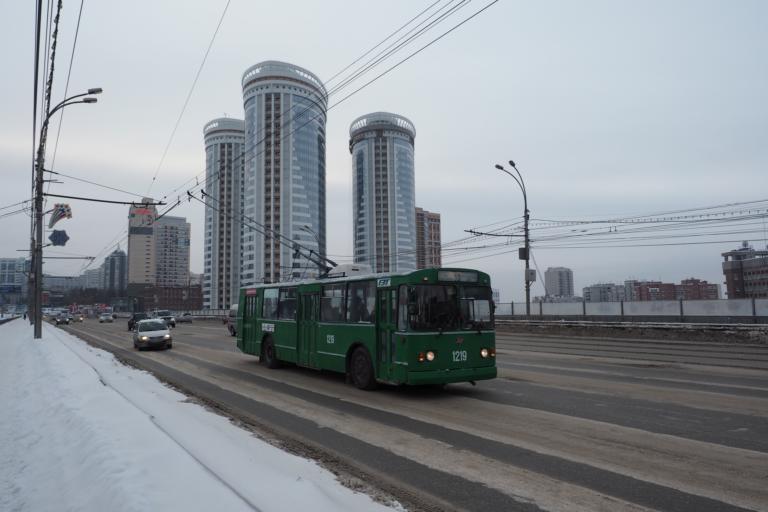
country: RU
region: Novosibirsk
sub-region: Novosibirskiy Rayon
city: Novosibirsk
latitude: 55.0231
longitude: 82.9313
